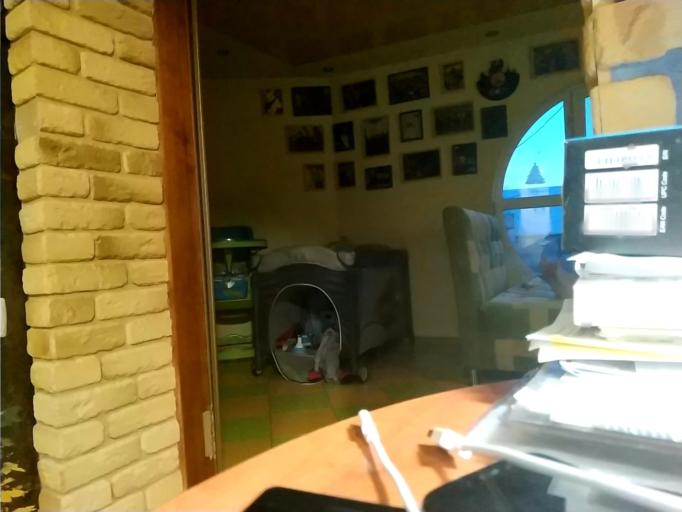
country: RU
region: Republic of Karelia
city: Belomorsk
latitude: 64.4274
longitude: 34.6805
